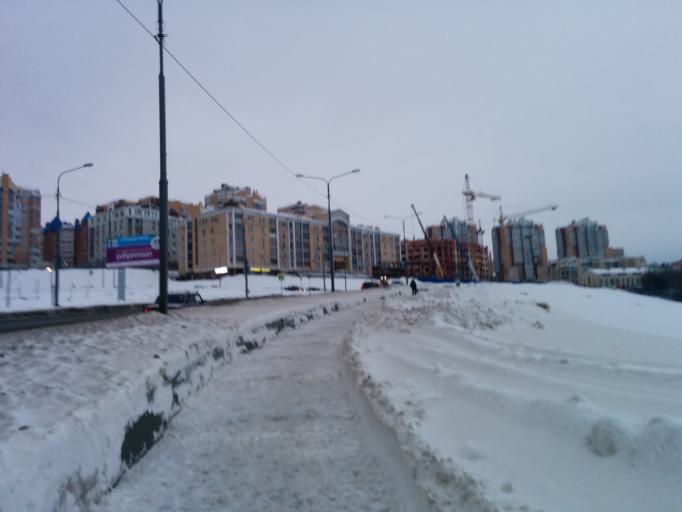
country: RU
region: Chuvashia
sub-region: Cheboksarskiy Rayon
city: Cheboksary
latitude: 56.1387
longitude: 47.2322
